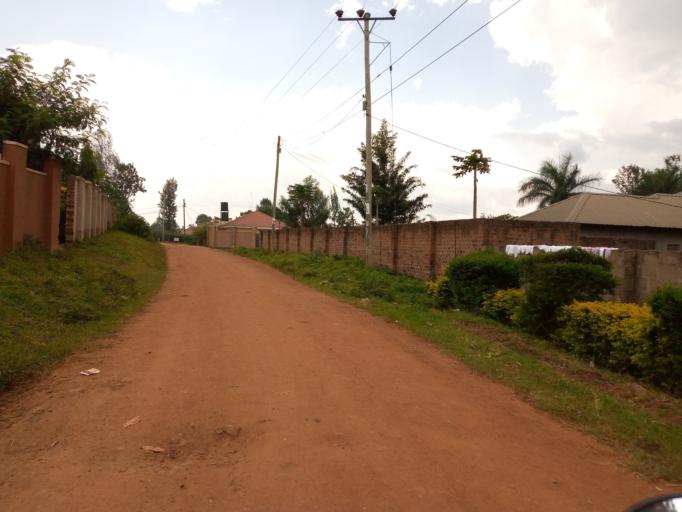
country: UG
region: Eastern Region
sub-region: Mbale District
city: Mbale
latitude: 1.0891
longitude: 34.1703
